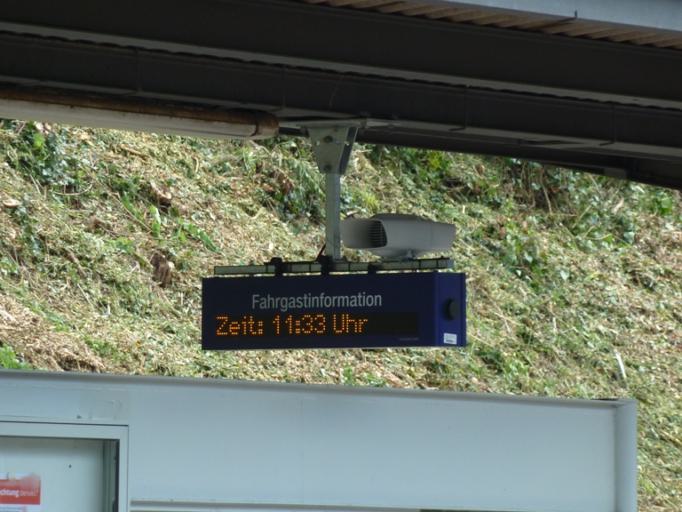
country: DE
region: Baden-Wuerttemberg
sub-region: Tuebingen Region
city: Uberlingen
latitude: 47.7693
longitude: 9.1454
